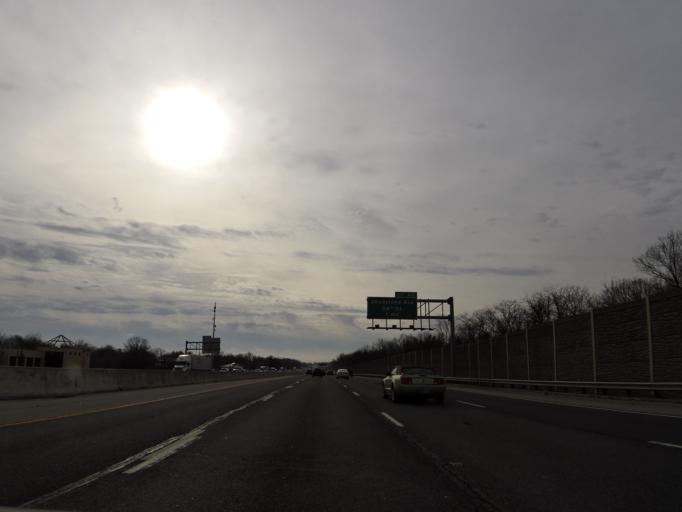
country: US
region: Indiana
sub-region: Marion County
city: Lawrence
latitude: 39.8831
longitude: -86.0478
